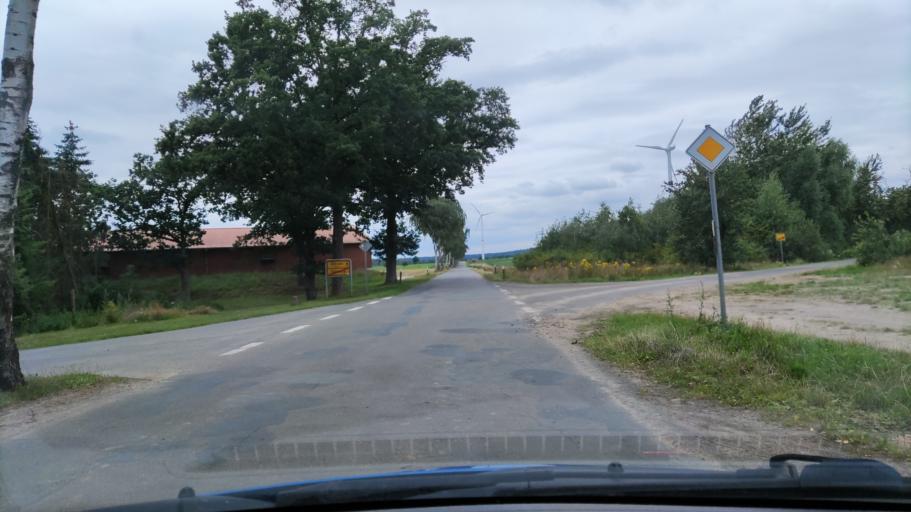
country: DE
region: Lower Saxony
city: Oetzen
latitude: 53.0202
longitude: 10.7088
